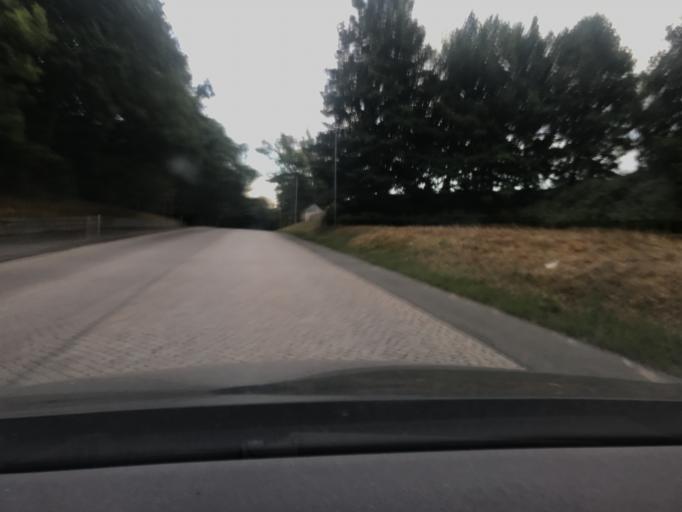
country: SE
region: Skane
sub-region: Simrishamns Kommun
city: Simrishamn
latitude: 55.5676
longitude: 14.3341
